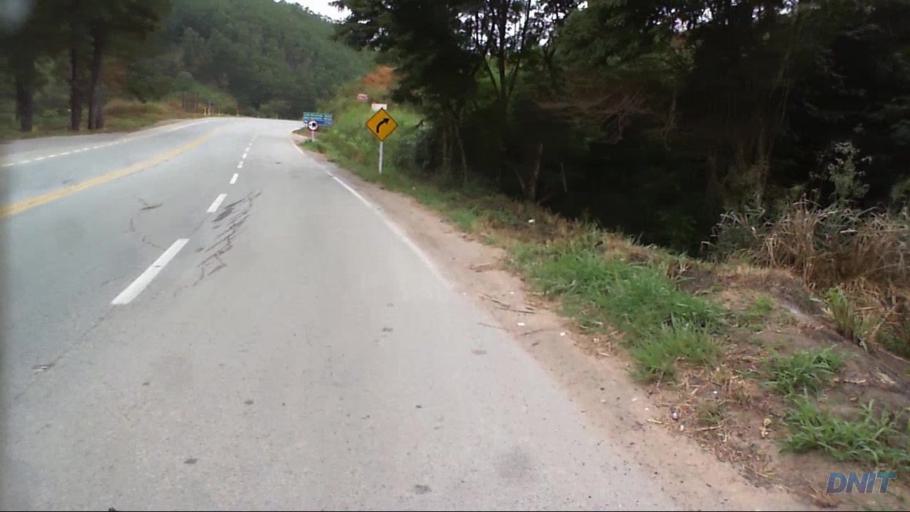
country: BR
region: Minas Gerais
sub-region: Nova Era
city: Nova Era
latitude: -19.7762
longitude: -43.0450
